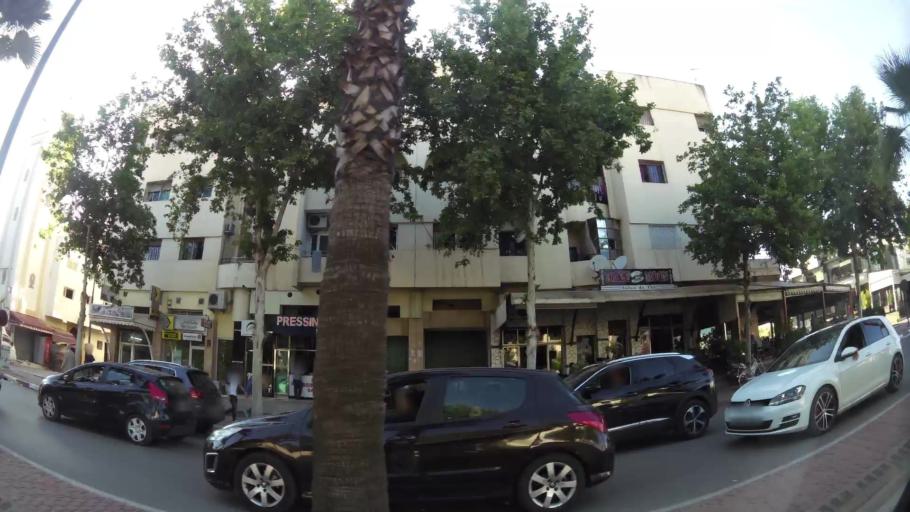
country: MA
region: Fes-Boulemane
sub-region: Fes
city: Fes
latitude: 34.0194
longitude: -5.0182
